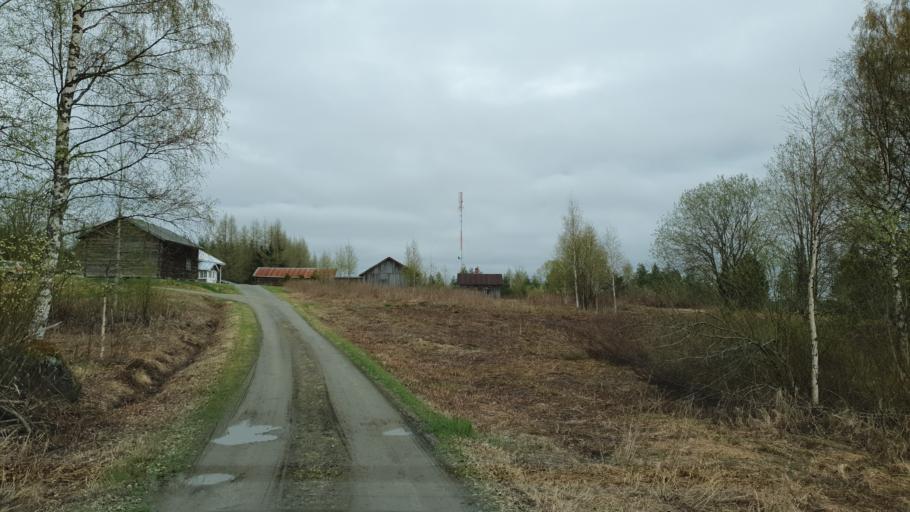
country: FI
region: Kainuu
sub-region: Kehys-Kainuu
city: Kuhmo
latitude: 64.1386
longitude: 29.9699
